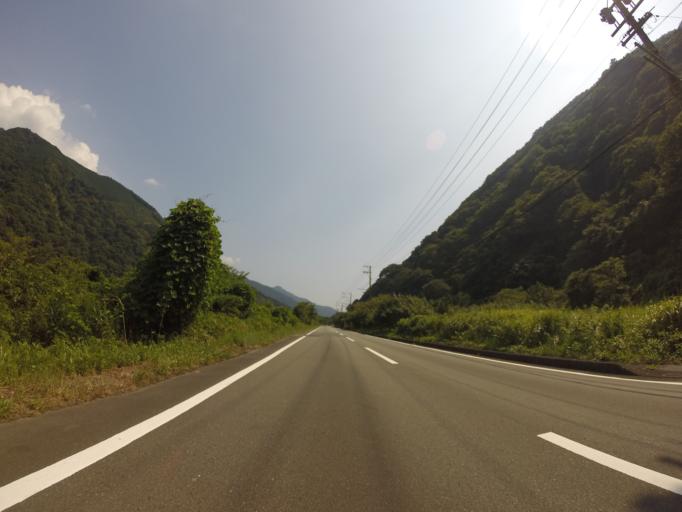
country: JP
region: Shizuoka
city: Shizuoka-shi
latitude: 35.1637
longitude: 138.3621
